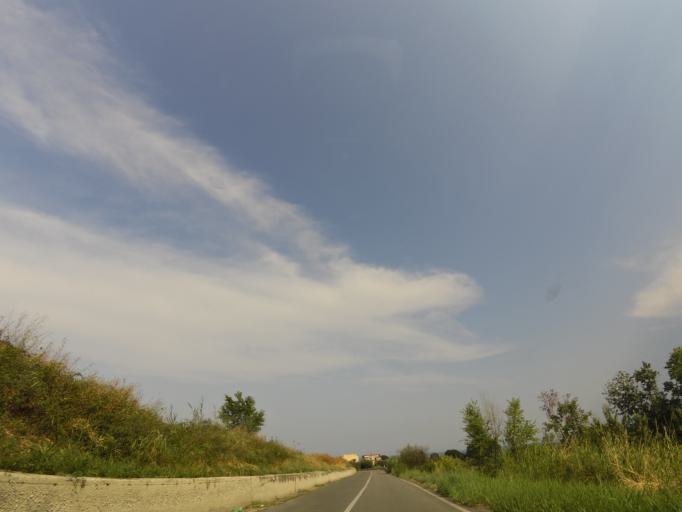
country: IT
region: Calabria
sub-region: Provincia di Reggio Calabria
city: Monasterace
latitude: 38.4397
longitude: 16.5462
